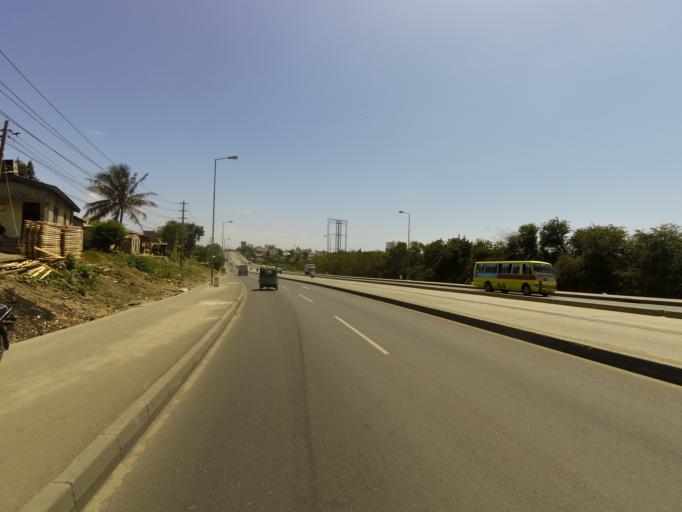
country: TZ
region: Dar es Salaam
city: Magomeni
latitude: -6.8032
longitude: 39.2614
